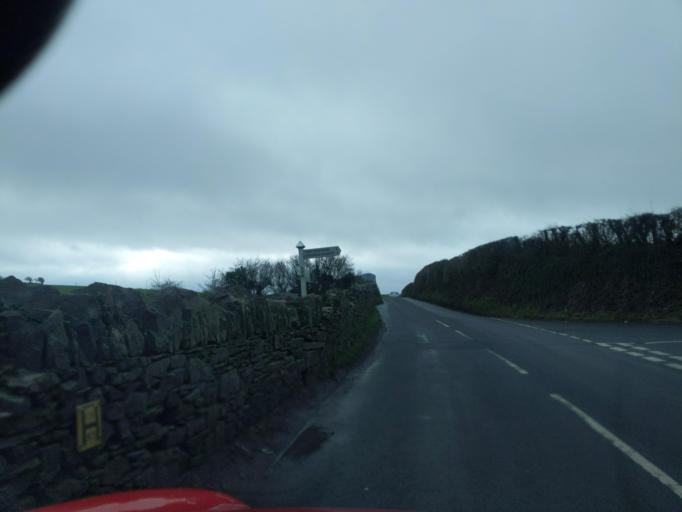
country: GB
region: England
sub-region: Plymouth
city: Plymstock
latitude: 50.3421
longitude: -4.0910
